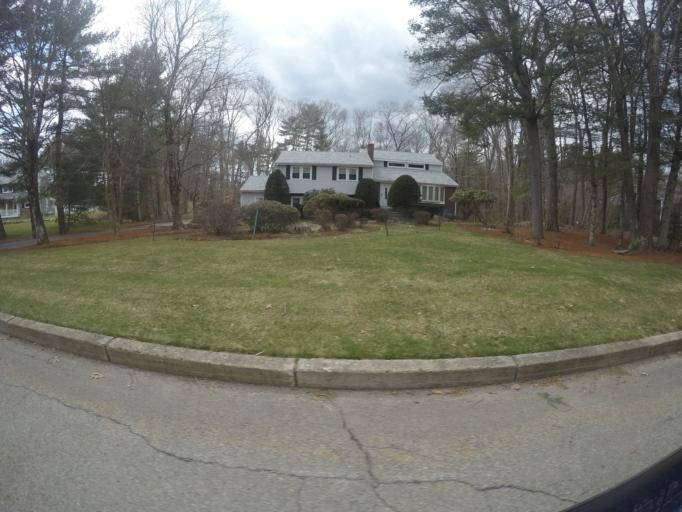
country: US
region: Massachusetts
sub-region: Bristol County
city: Easton
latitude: 42.0472
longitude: -71.1358
